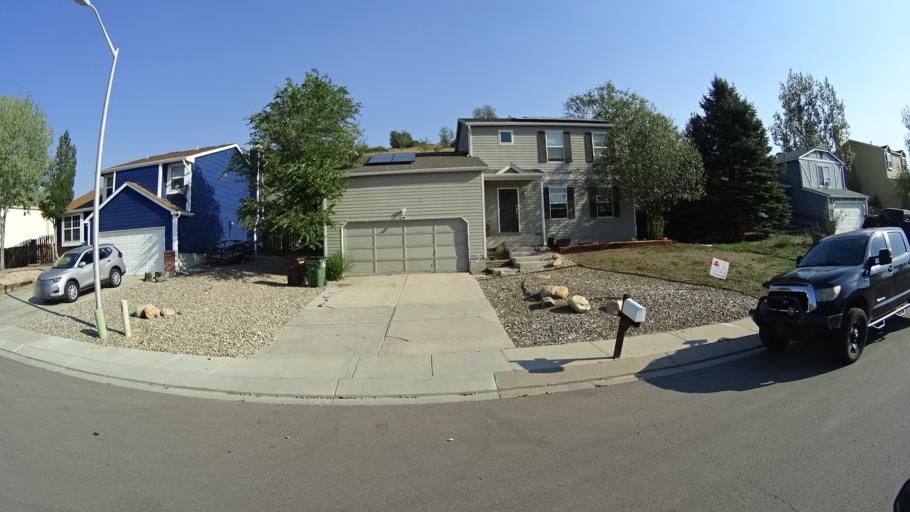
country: US
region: Colorado
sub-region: El Paso County
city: Stratmoor
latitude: 38.7798
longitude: -104.8154
